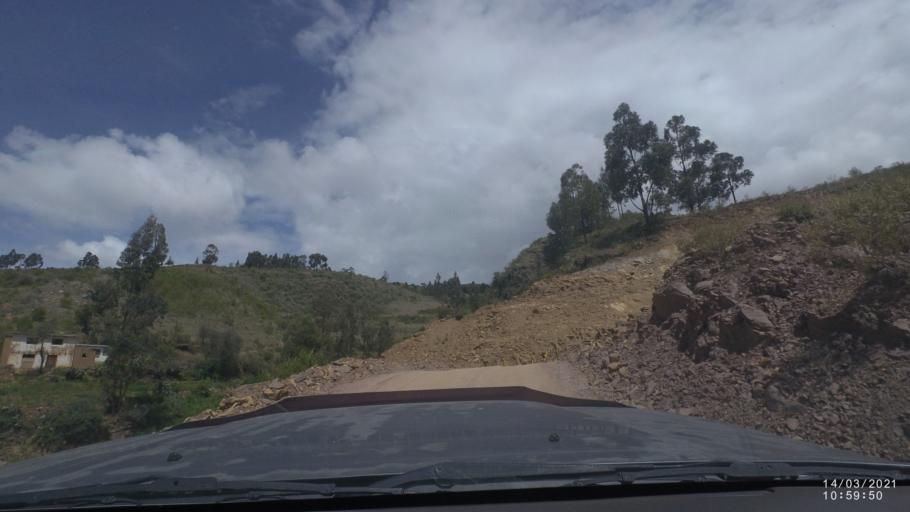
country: BO
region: Cochabamba
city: Tarata
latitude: -17.8073
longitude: -65.9631
